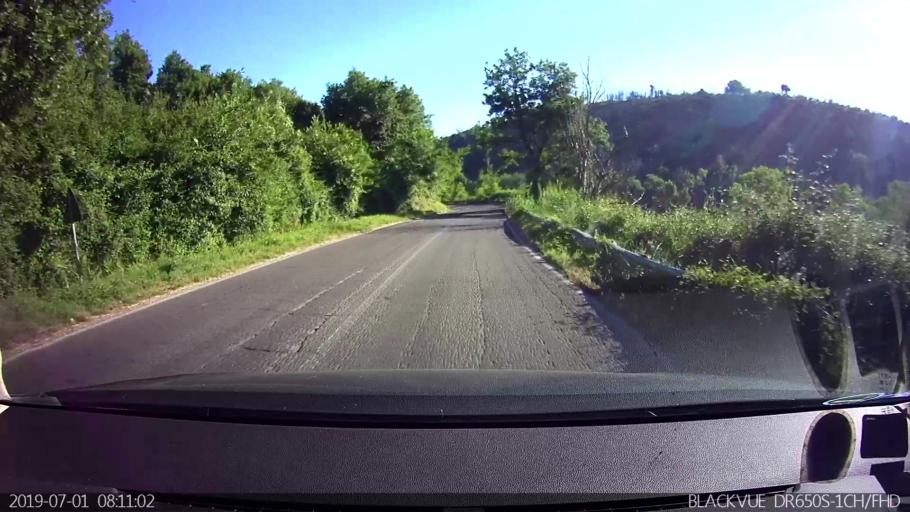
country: IT
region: Latium
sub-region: Provincia di Frosinone
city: Sant'Angelo in Villa-Giglio
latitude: 41.6748
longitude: 13.4217
